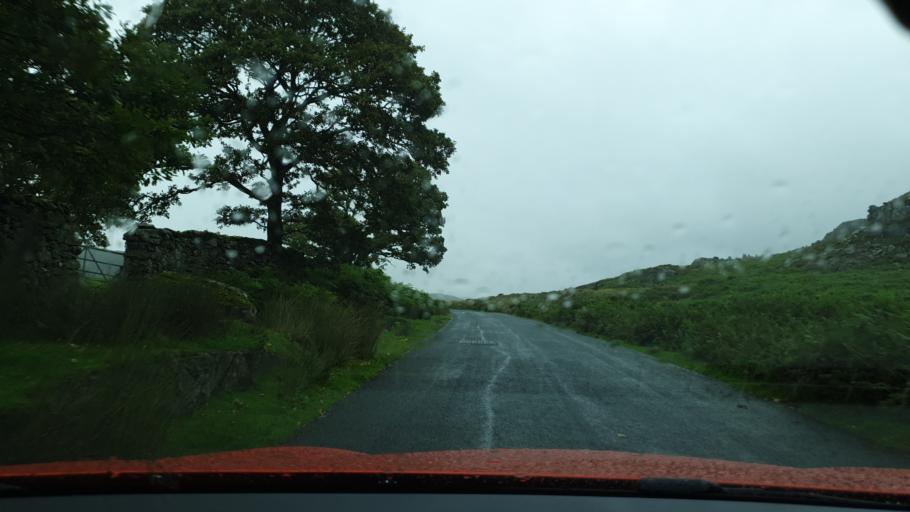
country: GB
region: England
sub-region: Cumbria
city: Millom
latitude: 54.3220
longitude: -3.2356
